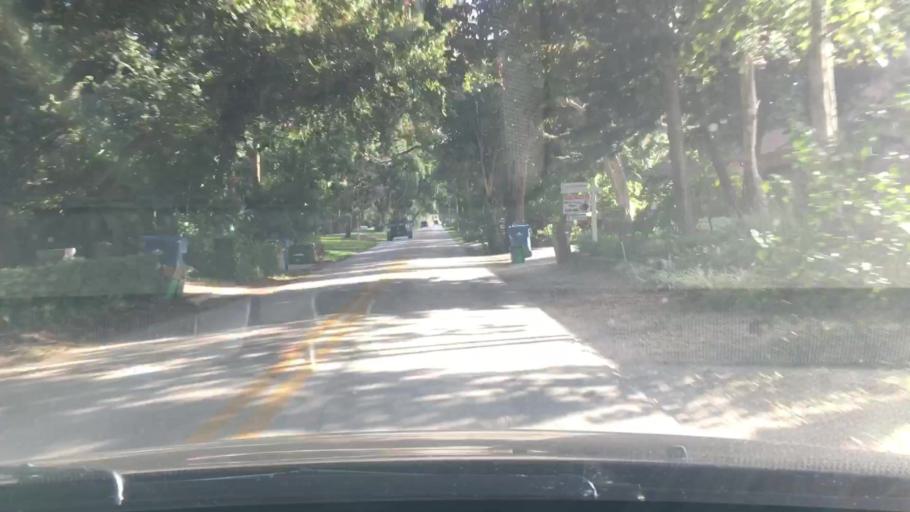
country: US
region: Florida
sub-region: Volusia County
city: Ormond-by-the-Sea
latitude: 29.3628
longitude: -81.0795
